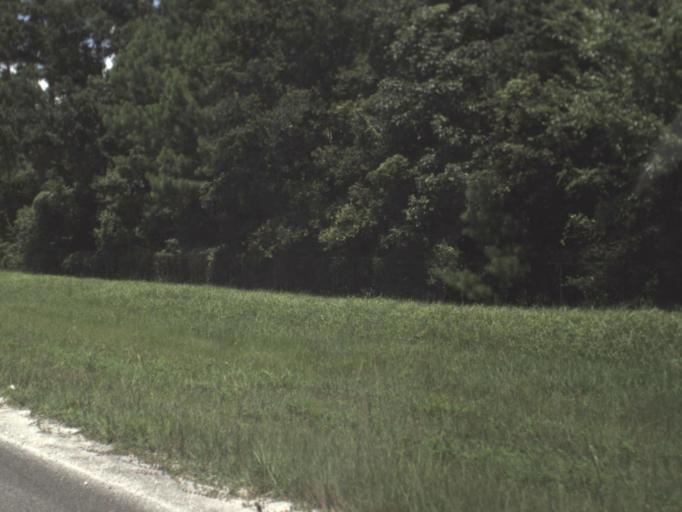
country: US
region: Florida
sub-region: Hernando County
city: Brooksville
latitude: 28.5384
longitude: -82.3852
